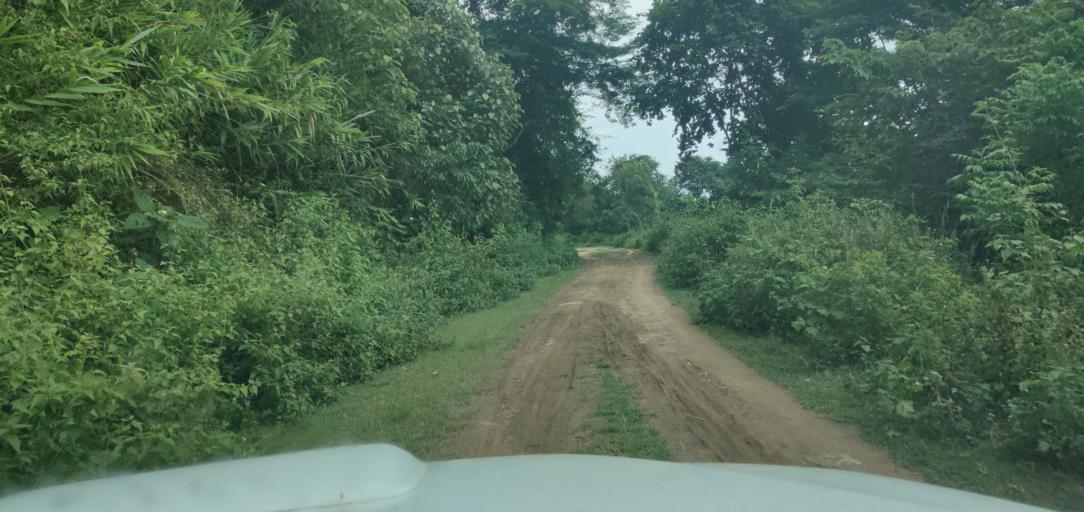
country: LA
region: Phongsali
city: Phongsali
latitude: 21.4471
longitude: 102.3146
